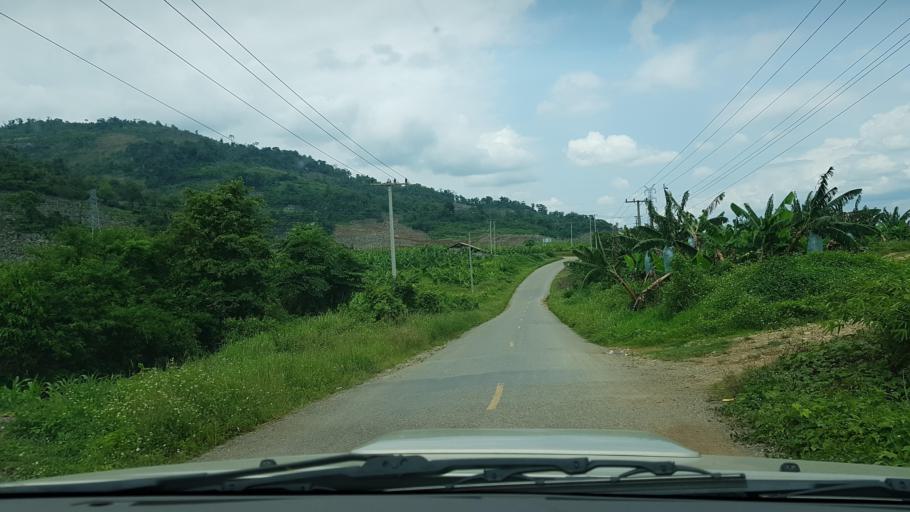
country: TH
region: Nan
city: Chaloem Phra Kiat
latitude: 19.9981
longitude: 101.2843
